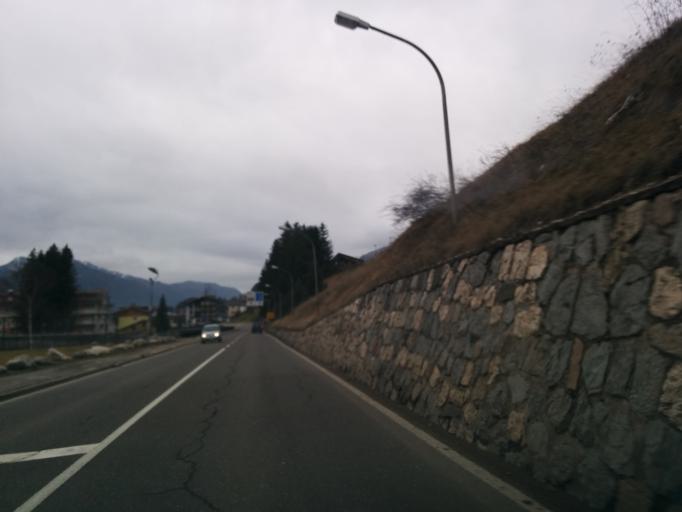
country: IT
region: Trentino-Alto Adige
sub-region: Provincia di Trento
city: Pozza di Fassa
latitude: 46.4328
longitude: 11.6871
